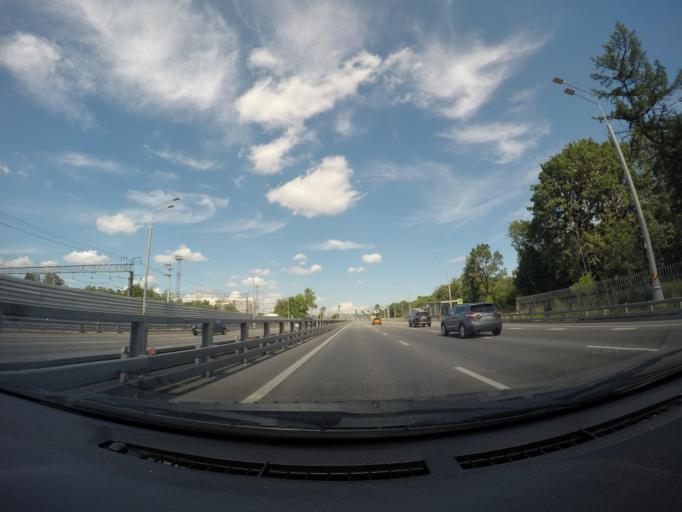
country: RU
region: Moscow
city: Ryazanskiy
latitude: 55.7298
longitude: 37.7783
